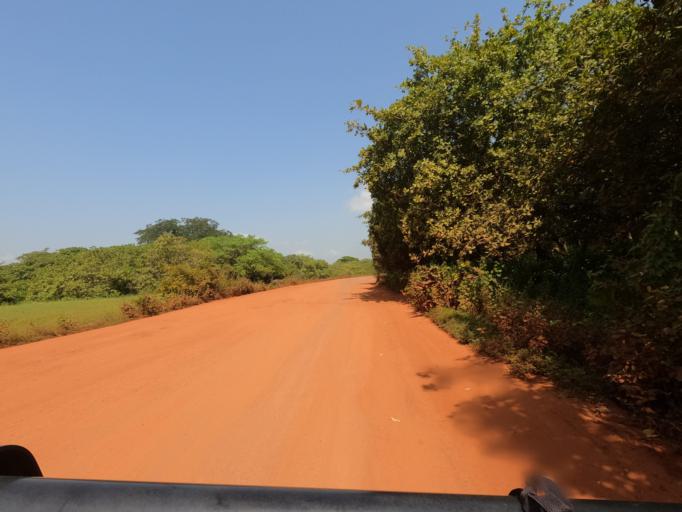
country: GW
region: Cacheu
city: Canchungo
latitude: 12.2686
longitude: -15.7879
